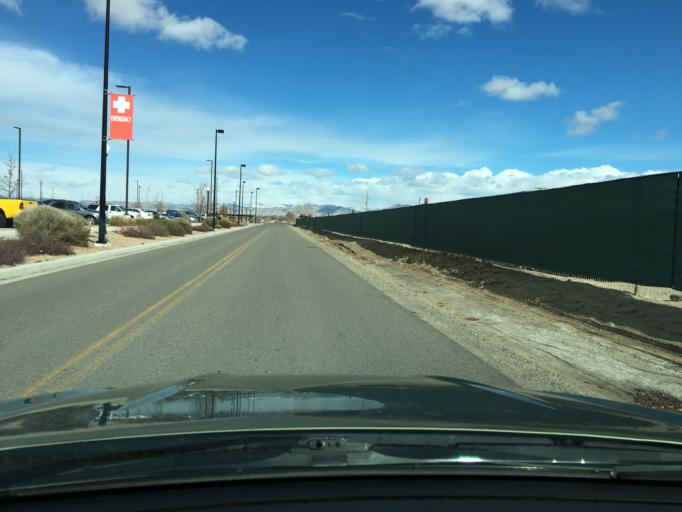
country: US
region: Colorado
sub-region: Mesa County
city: Redlands
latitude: 39.1046
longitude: -108.6128
